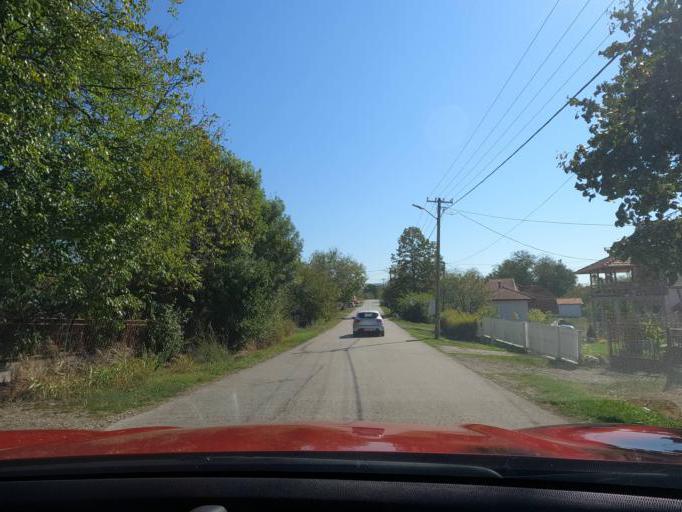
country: RS
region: Central Serbia
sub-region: Raski Okrug
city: Kraljevo
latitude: 43.7537
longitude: 20.6971
